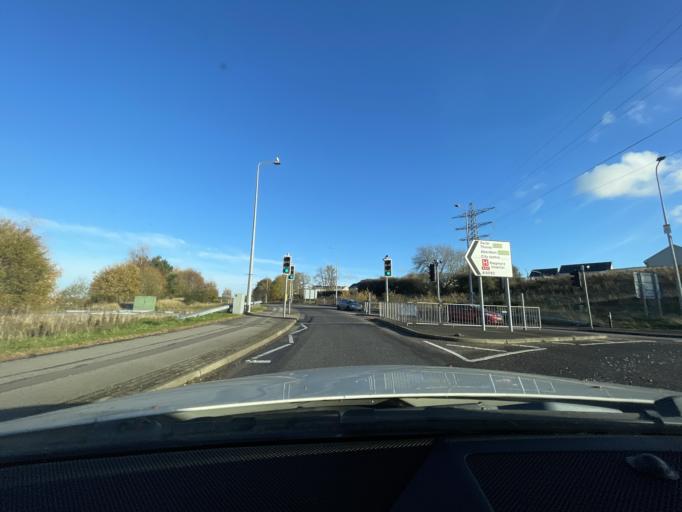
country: GB
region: Scotland
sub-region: Highland
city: Inverness
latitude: 57.4479
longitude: -4.2224
